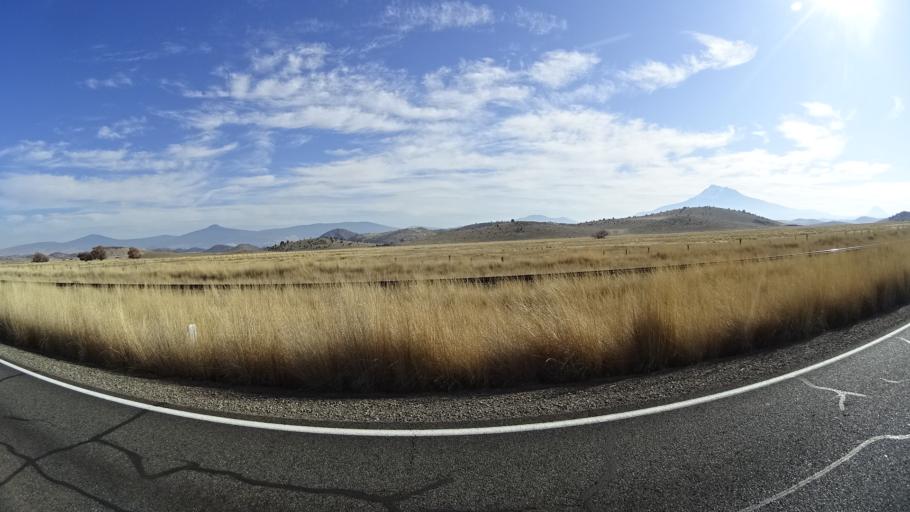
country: US
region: California
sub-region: Siskiyou County
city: Montague
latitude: 41.5928
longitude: -122.5240
